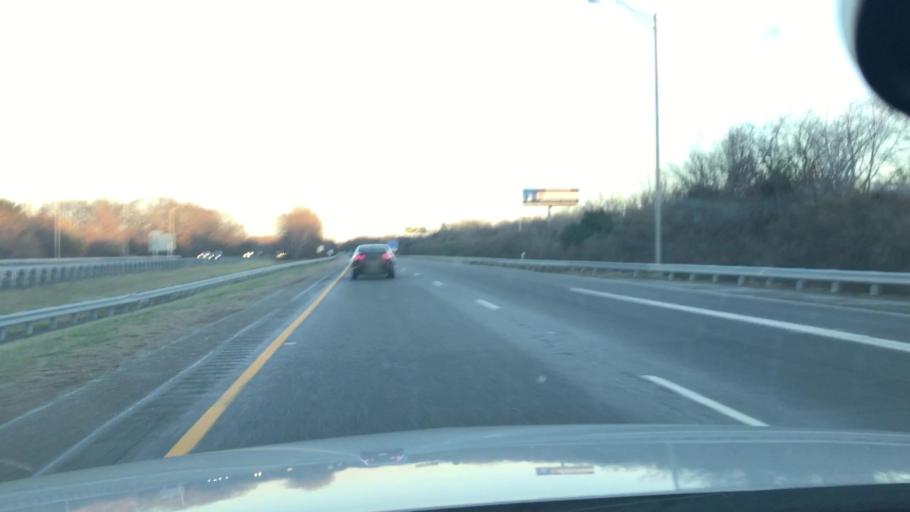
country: US
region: New Jersey
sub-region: Camden County
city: Sicklerville
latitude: 39.7305
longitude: -75.0061
